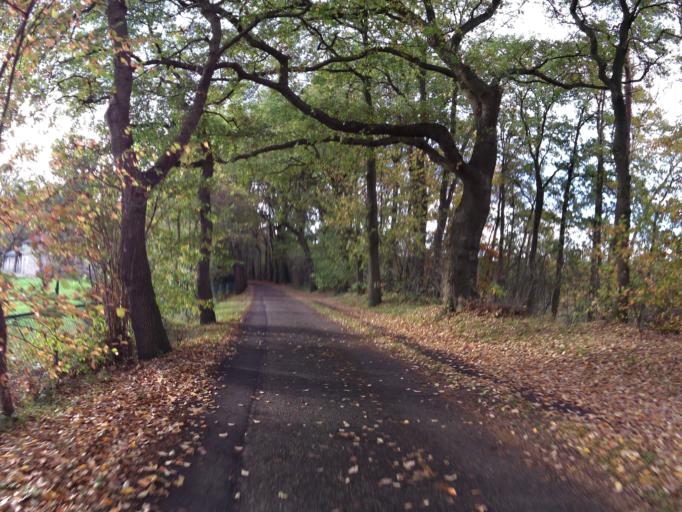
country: NL
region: North Brabant
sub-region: Gemeente Vught
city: Vught
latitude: 51.6505
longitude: 5.2433
